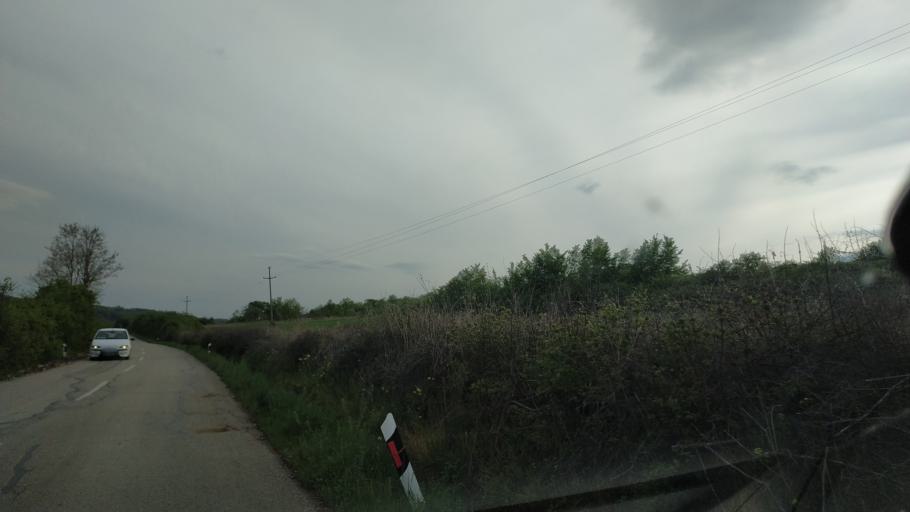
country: RS
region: Central Serbia
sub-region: Zajecarski Okrug
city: Soko Banja
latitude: 43.5122
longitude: 21.8439
